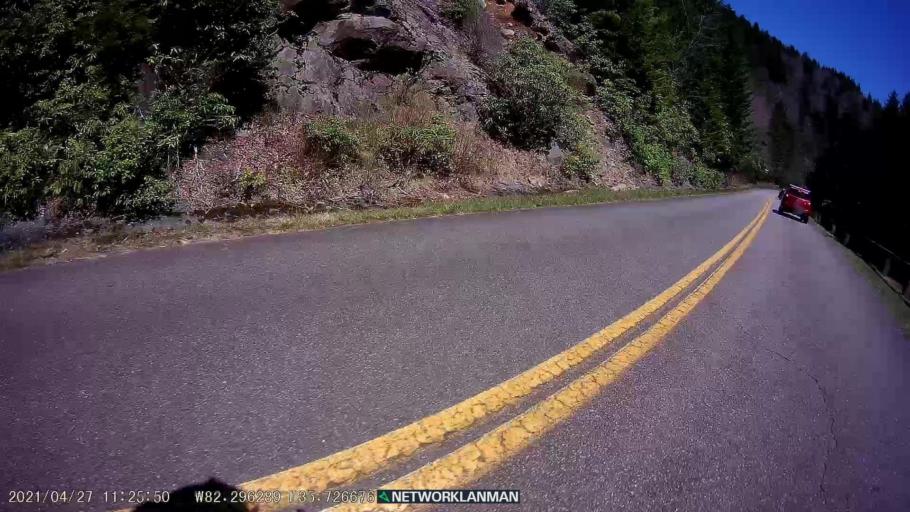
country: US
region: North Carolina
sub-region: Buncombe County
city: Black Mountain
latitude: 35.7266
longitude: -82.2961
